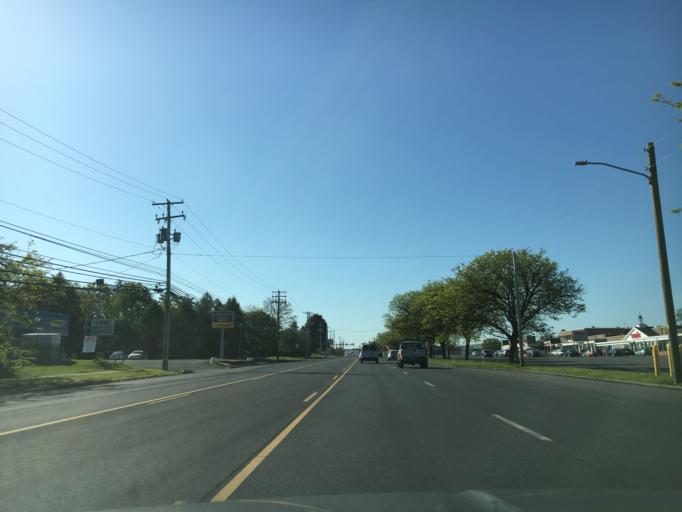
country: US
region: Pennsylvania
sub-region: Northampton County
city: Bethlehem
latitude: 40.6430
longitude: -75.4031
